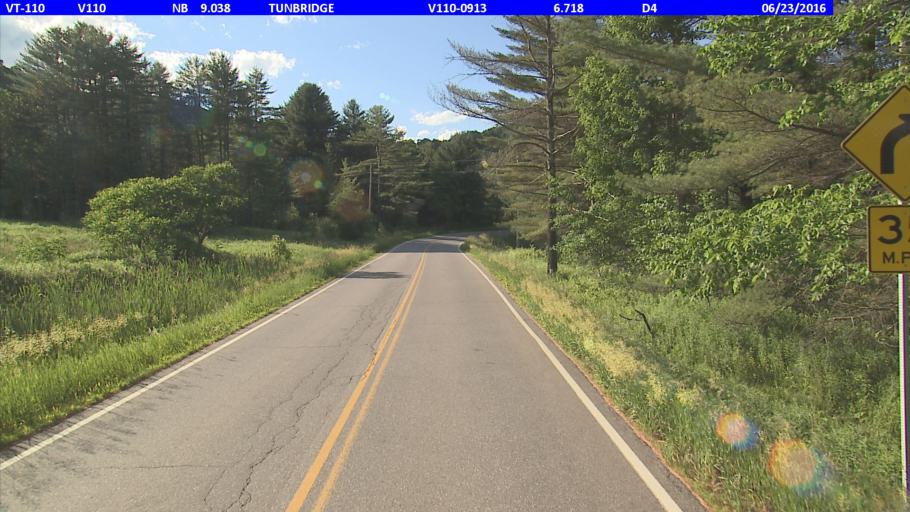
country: US
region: Vermont
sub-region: Orange County
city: Chelsea
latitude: 43.9362
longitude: -72.4671
